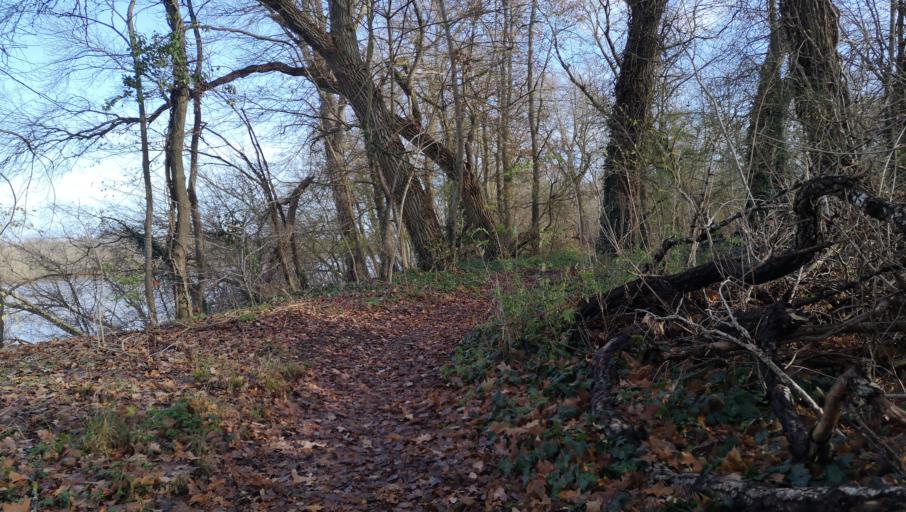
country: FR
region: Centre
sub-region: Departement du Loiret
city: Saint-Hilaire-Saint-Mesmin
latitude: 47.8680
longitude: 1.8121
